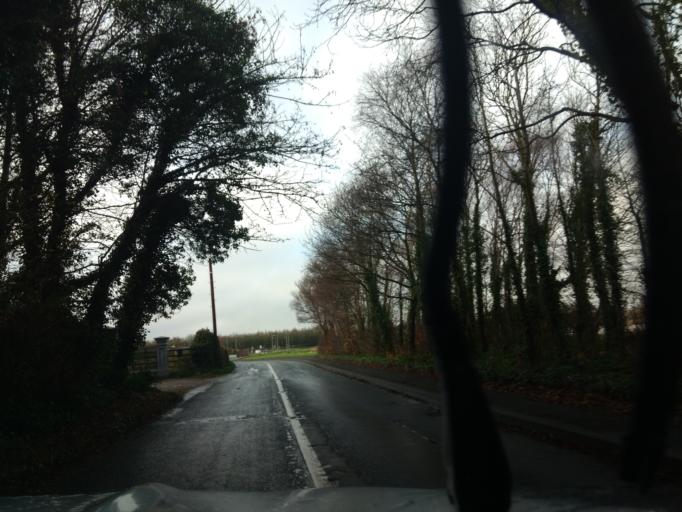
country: IE
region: Leinster
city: Kinsealy-Drinan
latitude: 53.4626
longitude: -6.1975
